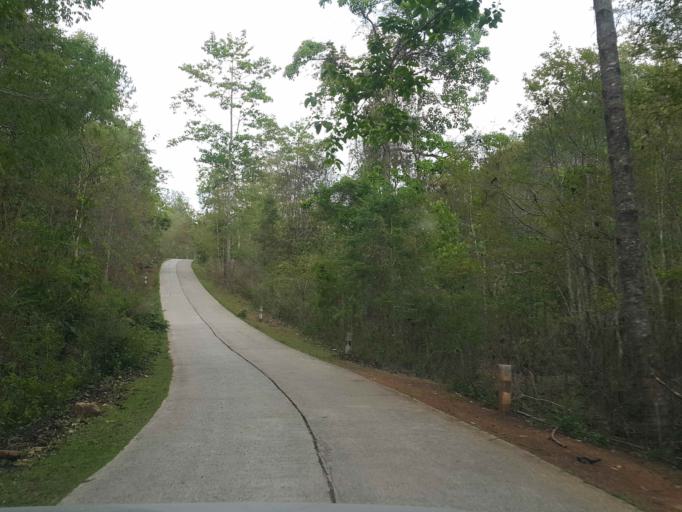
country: TH
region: Chiang Mai
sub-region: Amphoe Chiang Dao
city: Chiang Dao
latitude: 19.3778
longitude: 98.7651
